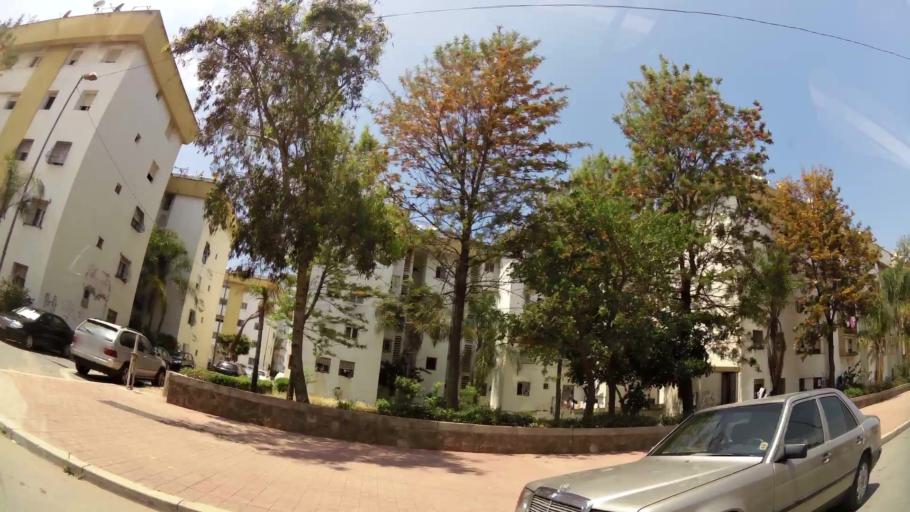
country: MA
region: Rabat-Sale-Zemmour-Zaer
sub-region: Skhirate-Temara
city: Temara
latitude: 33.9712
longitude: -6.8975
